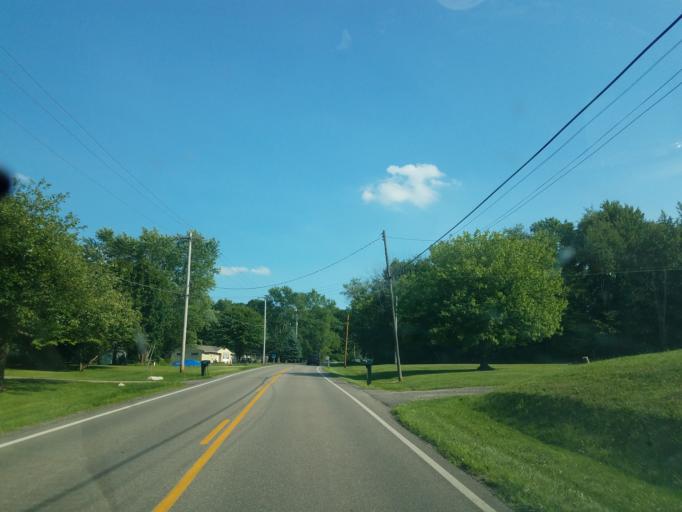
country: US
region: Ohio
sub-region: Stark County
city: Greentown
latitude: 40.9363
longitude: -81.4300
